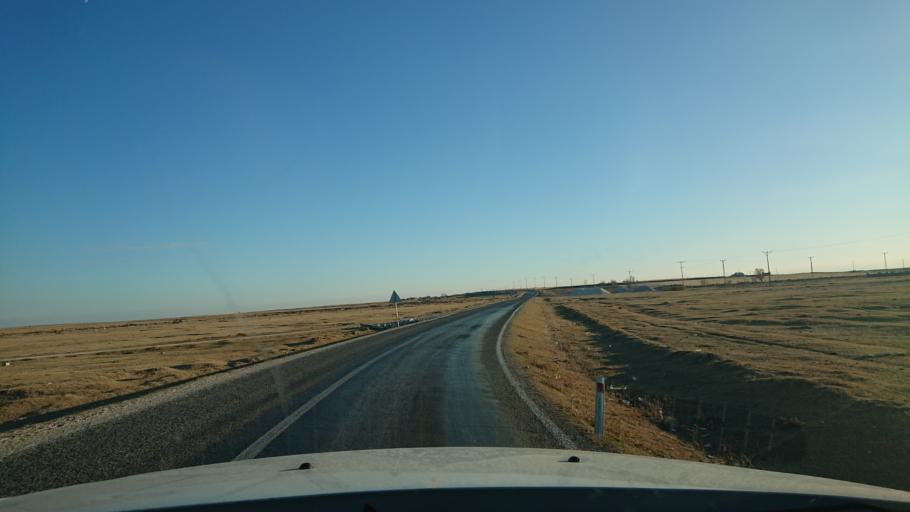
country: TR
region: Aksaray
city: Eskil
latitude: 38.5548
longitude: 33.2005
